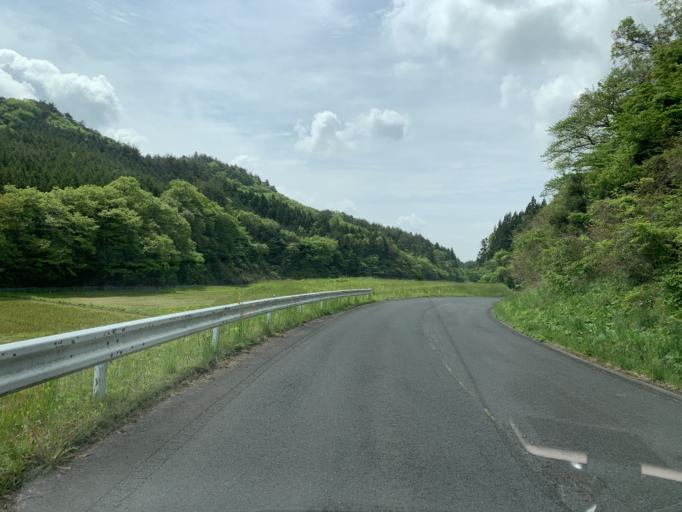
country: JP
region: Iwate
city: Ichinoseki
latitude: 38.8823
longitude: 140.9747
